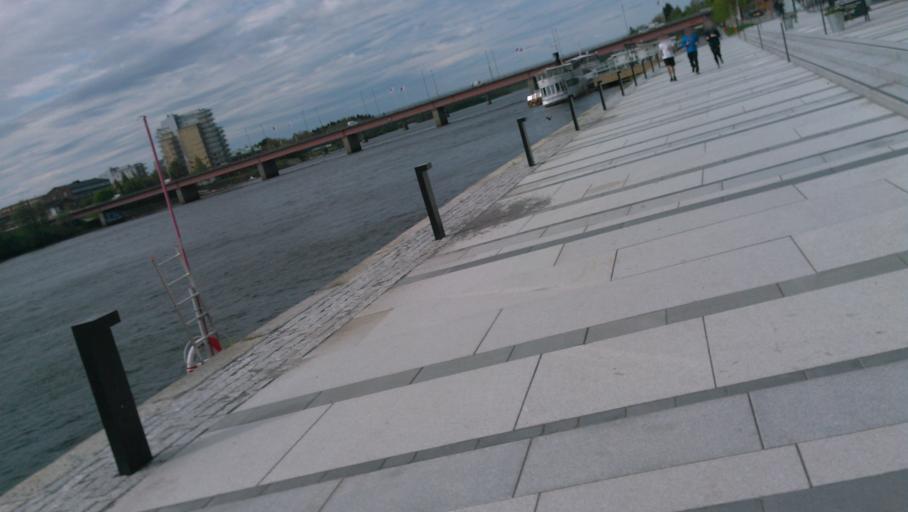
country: SE
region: Vaesterbotten
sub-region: Umea Kommun
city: Umea
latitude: 63.8240
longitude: 20.2606
